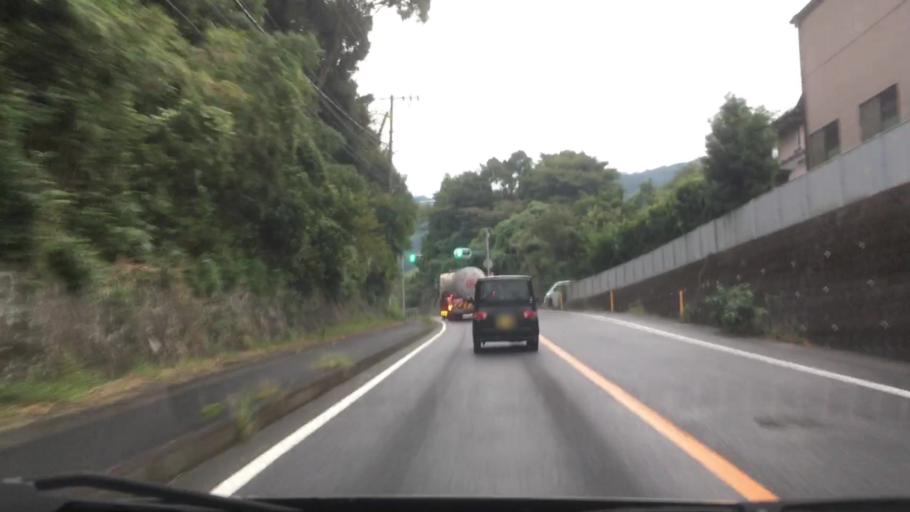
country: JP
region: Nagasaki
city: Sasebo
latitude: 33.1039
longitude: 129.7737
